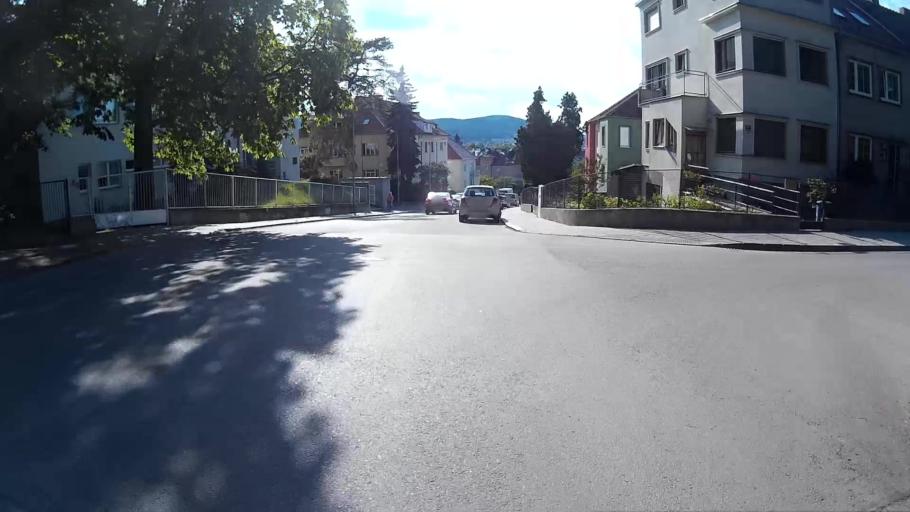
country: CZ
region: South Moravian
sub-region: Mesto Brno
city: Brno
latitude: 49.2085
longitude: 16.5778
